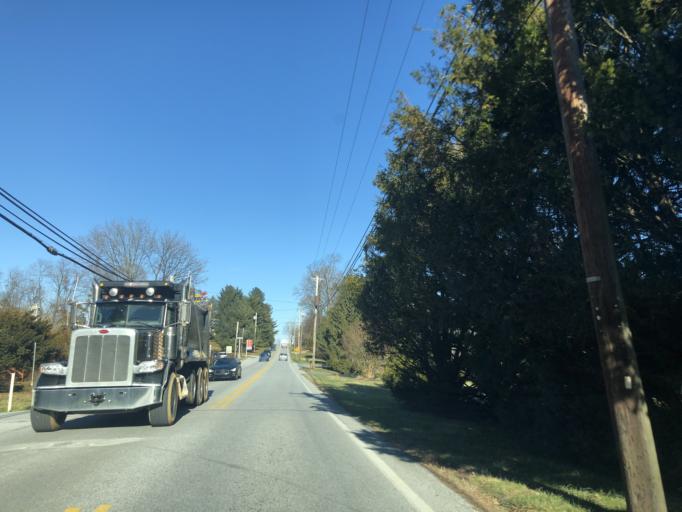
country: US
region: Pennsylvania
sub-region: Chester County
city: Kennett Square
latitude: 39.8634
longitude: -75.7165
